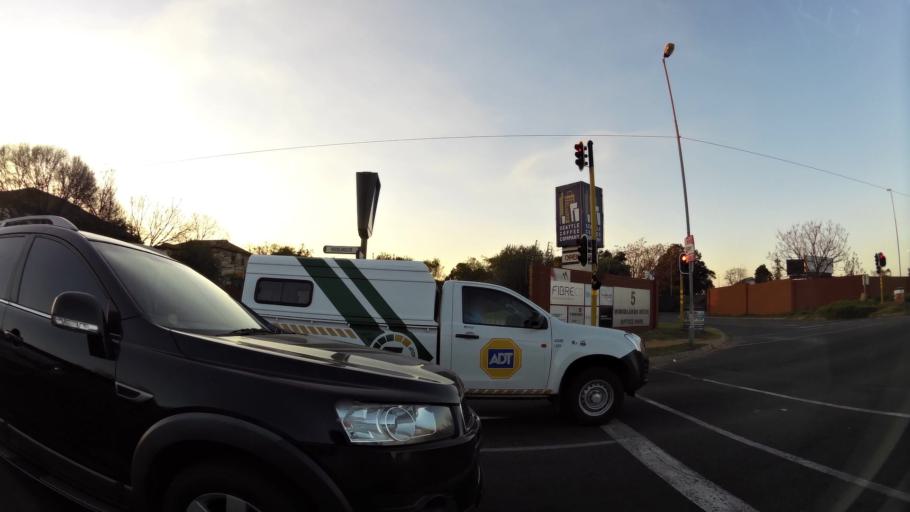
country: ZA
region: Gauteng
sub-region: City of Johannesburg Metropolitan Municipality
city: Midrand
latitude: -26.0567
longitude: 28.0889
